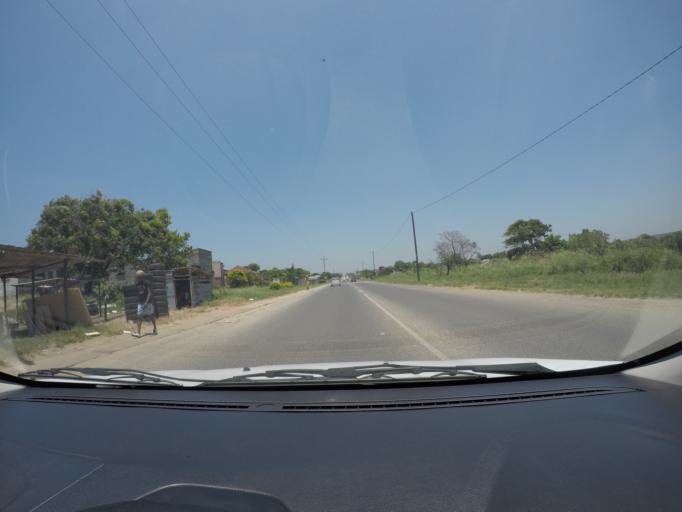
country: ZA
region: KwaZulu-Natal
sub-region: uThungulu District Municipality
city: eSikhawini
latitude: -28.8789
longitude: 31.9102
